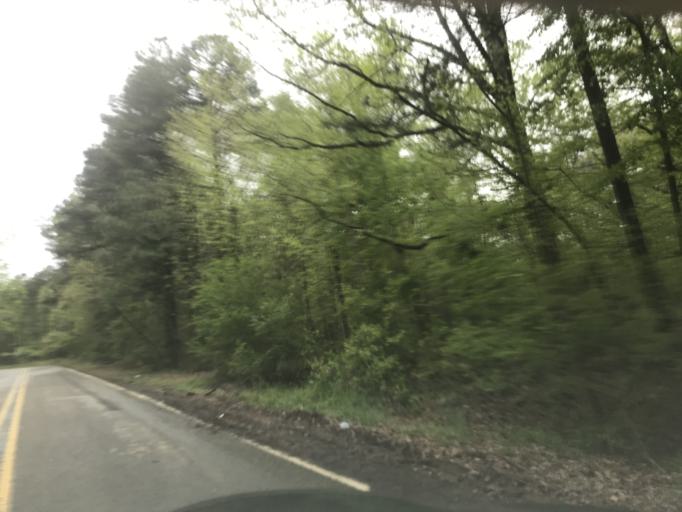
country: US
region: North Carolina
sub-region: Wake County
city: West Raleigh
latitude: 35.7593
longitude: -78.7043
